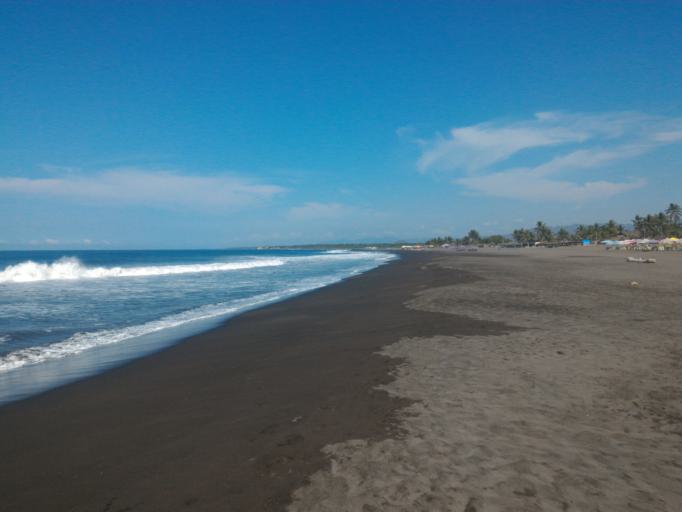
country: MX
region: Colima
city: Armeria
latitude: 18.8564
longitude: -103.9629
